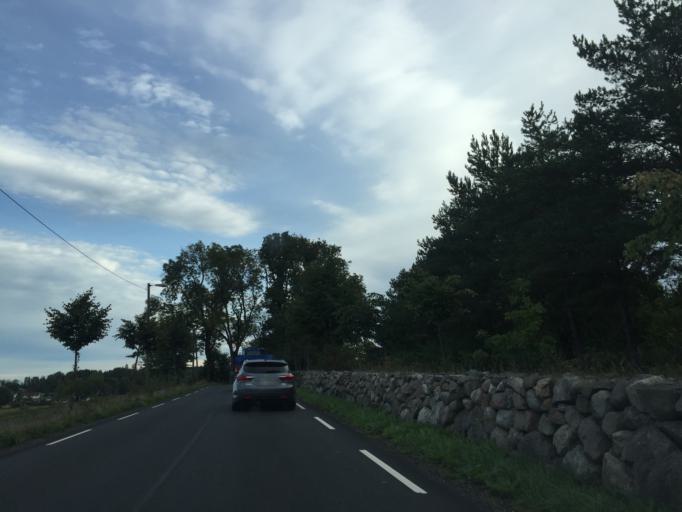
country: NO
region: Akershus
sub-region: As
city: As
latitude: 59.7138
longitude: 10.7736
